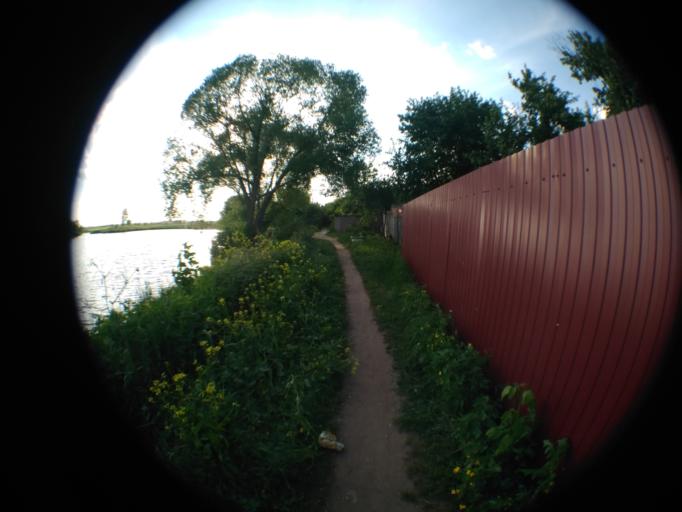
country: RU
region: Moskovskaya
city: Zhukovskiy
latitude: 55.5823
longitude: 38.1019
